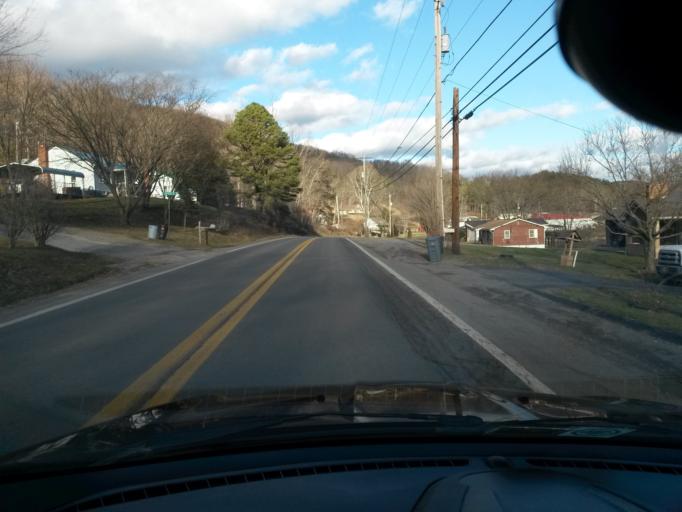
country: US
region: Virginia
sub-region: Giles County
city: Narrows
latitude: 37.3996
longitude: -80.7739
